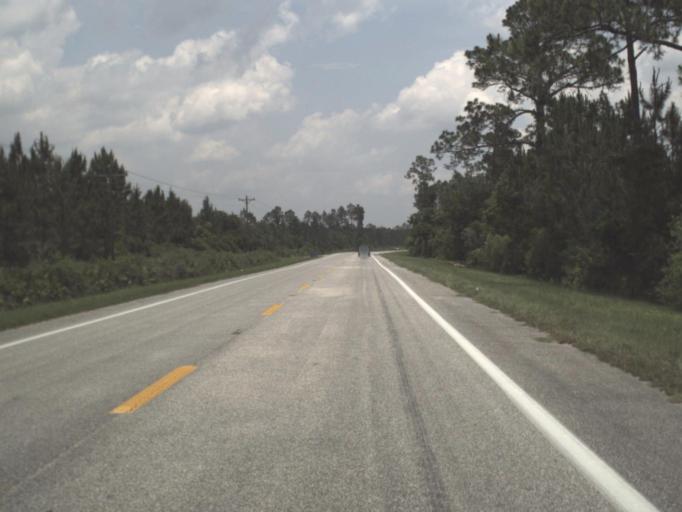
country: US
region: Florida
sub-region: Putnam County
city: Palatka
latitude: 29.5712
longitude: -81.7231
